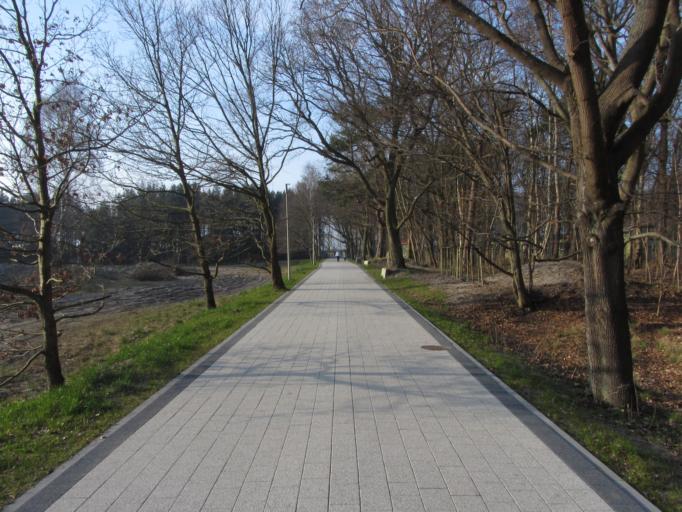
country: PL
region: West Pomeranian Voivodeship
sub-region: Powiat kolobrzeski
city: Kolobrzeg
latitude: 54.1765
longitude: 15.5359
